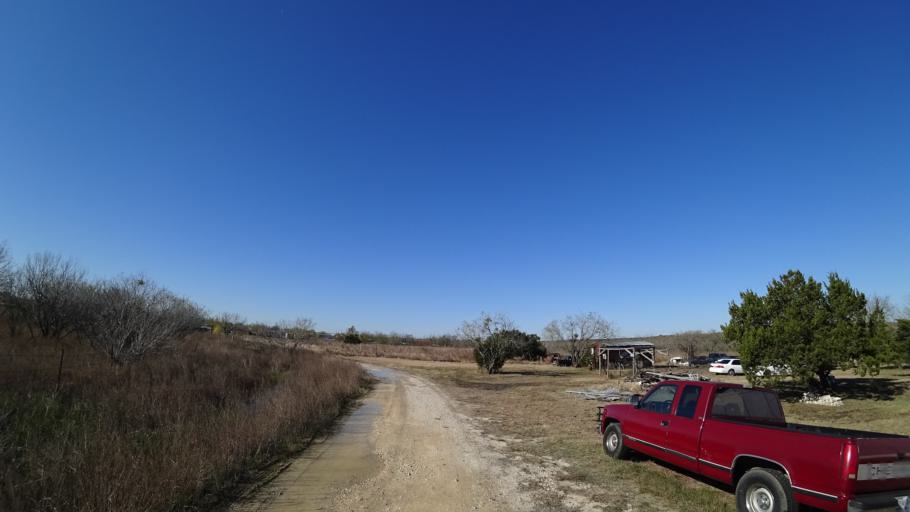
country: US
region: Texas
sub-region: Travis County
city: Onion Creek
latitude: 30.1059
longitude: -97.6776
